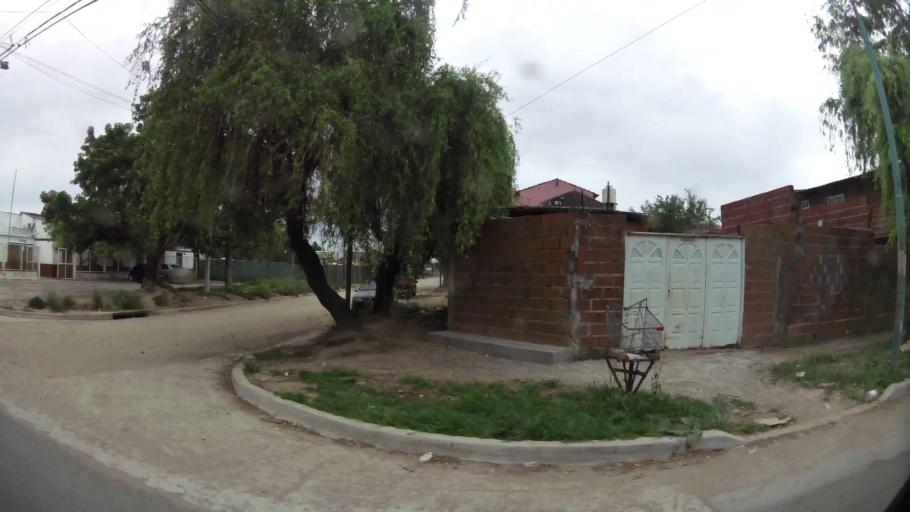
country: AR
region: Buenos Aires
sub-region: Partido de Zarate
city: Zarate
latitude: -34.1126
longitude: -59.0269
